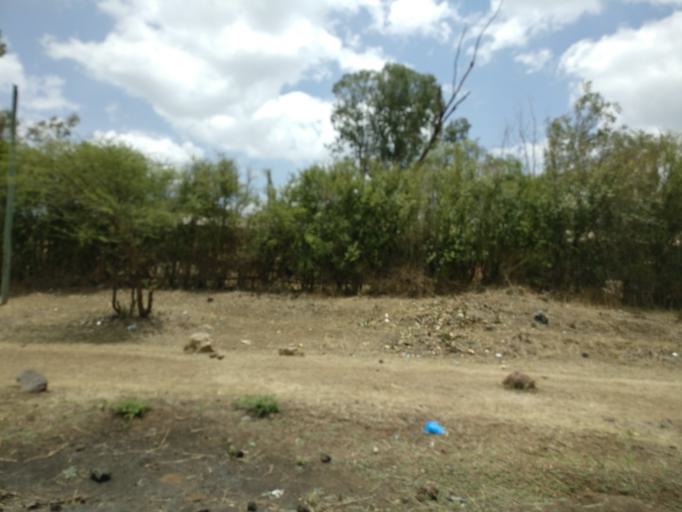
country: ET
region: Oromiya
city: Bishoftu
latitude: 8.7843
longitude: 38.9875
